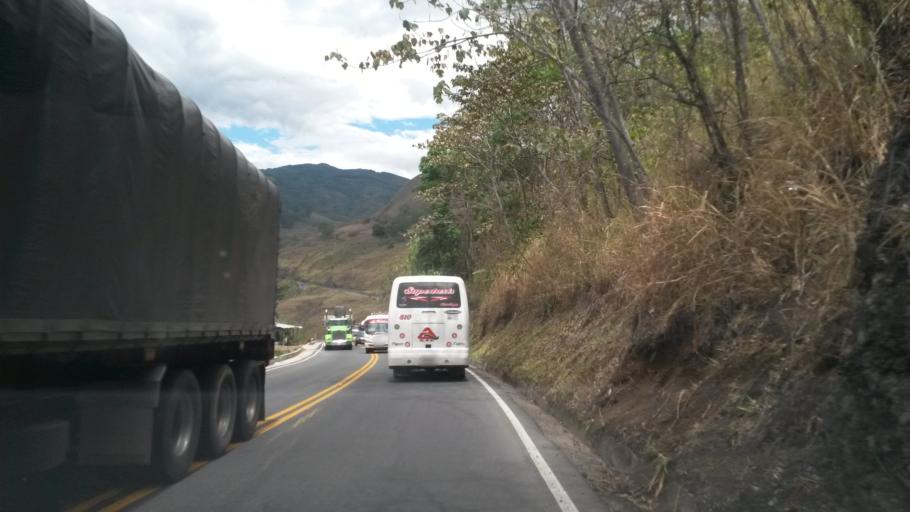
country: CO
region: Cauca
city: Rosas
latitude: 2.2806
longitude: -76.7138
